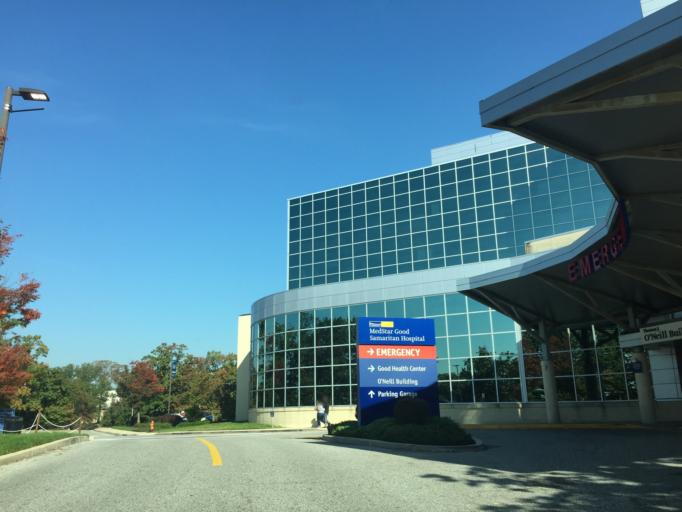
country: US
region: Maryland
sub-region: Baltimore County
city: Towson
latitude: 39.3584
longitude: -76.5881
